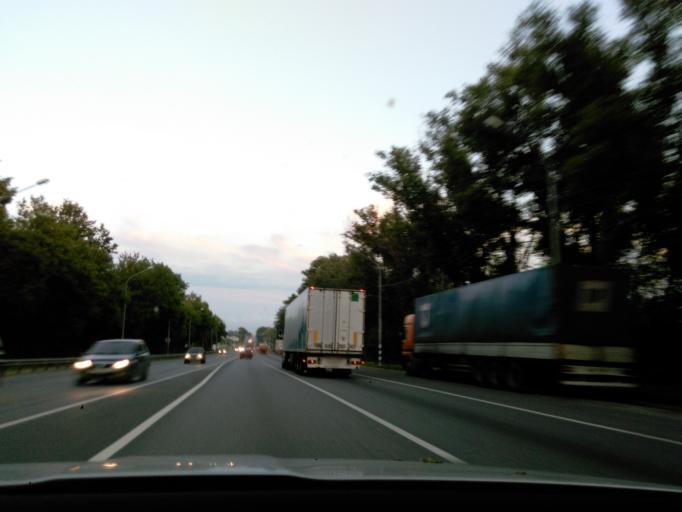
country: RU
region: Moskovskaya
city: Klin
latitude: 56.3627
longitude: 36.6914
